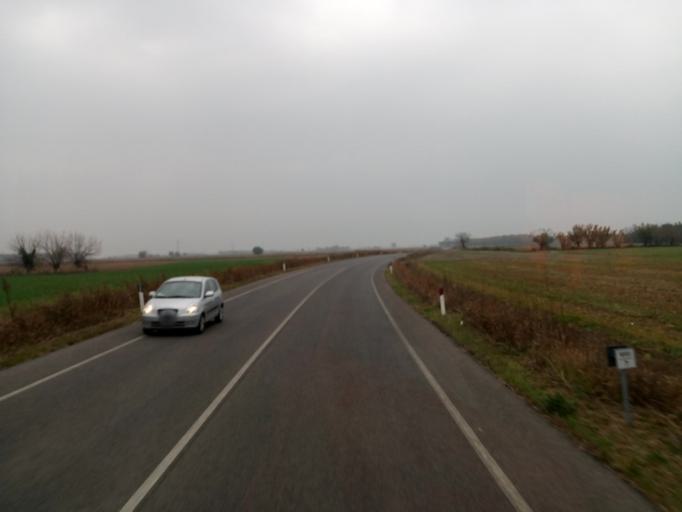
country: IT
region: Friuli Venezia Giulia
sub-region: Provincia di Udine
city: Orsaria
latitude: 46.0437
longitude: 13.3760
